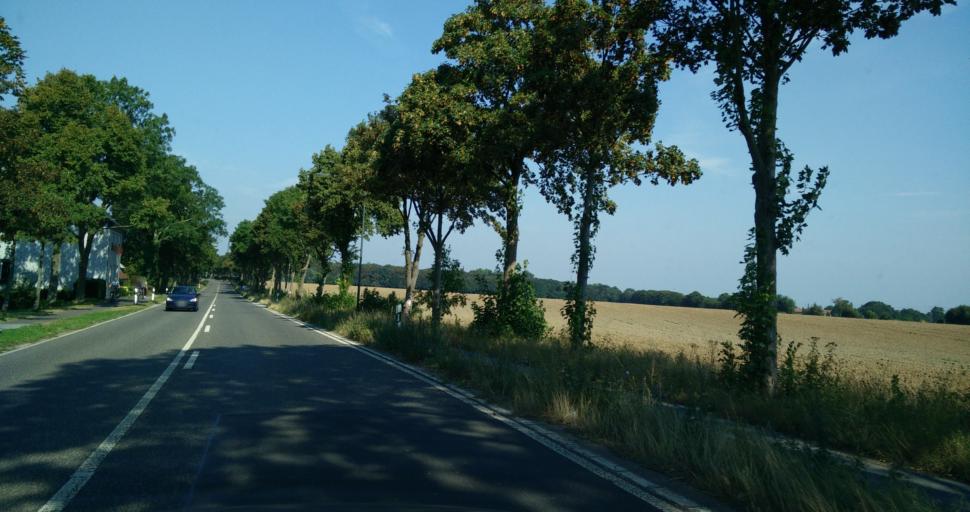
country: DE
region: North Rhine-Westphalia
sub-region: Regierungsbezirk Dusseldorf
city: Hochfeld
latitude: 51.3408
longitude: 6.7481
